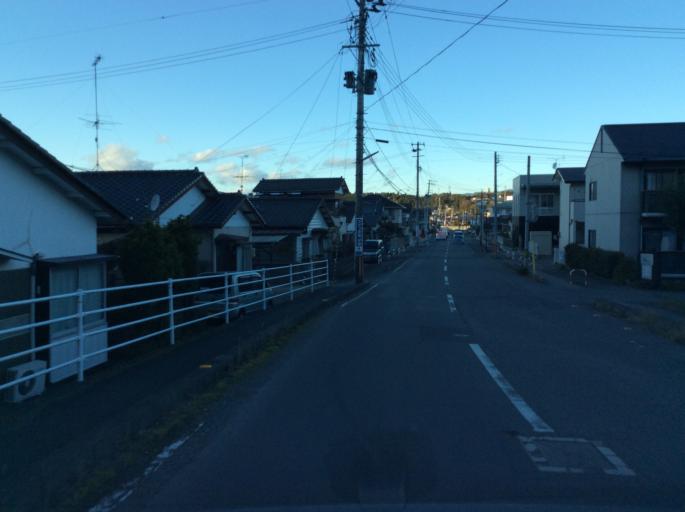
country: JP
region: Fukushima
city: Iwaki
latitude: 37.0570
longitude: 140.8678
